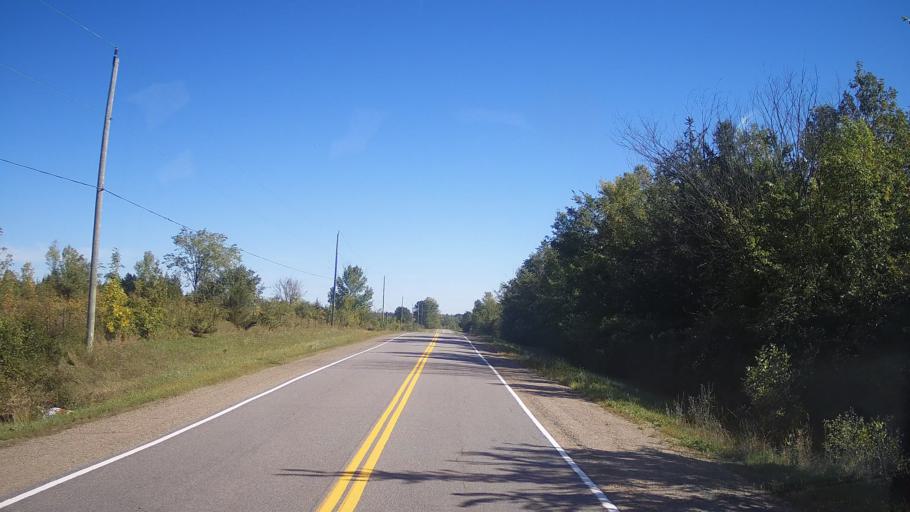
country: CA
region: Ontario
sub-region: Lanark County
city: Smiths Falls
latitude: 44.8056
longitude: -75.9702
